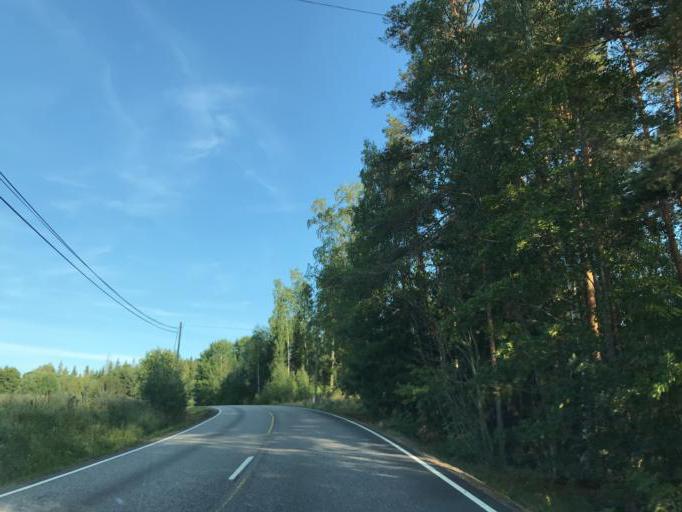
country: FI
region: Uusimaa
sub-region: Helsinki
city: Vihti
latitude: 60.4195
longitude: 24.3697
